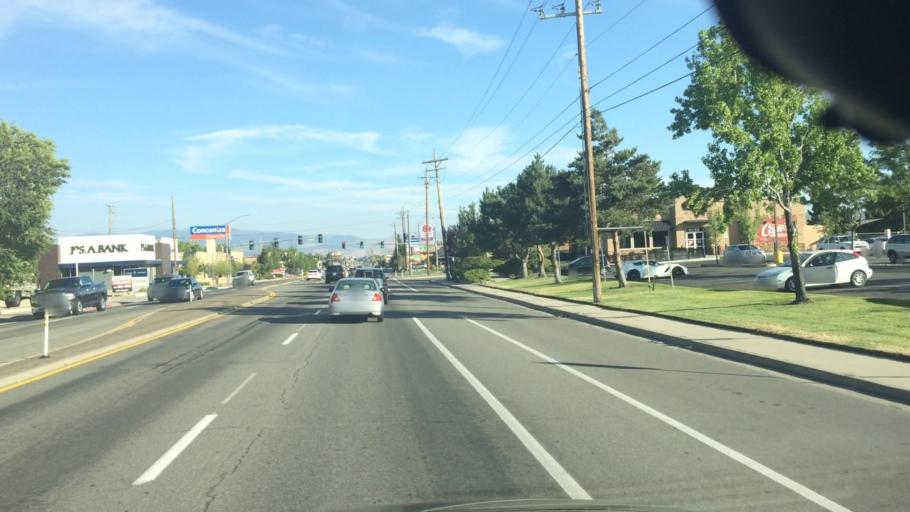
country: US
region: Nevada
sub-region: Washoe County
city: Reno
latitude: 39.4692
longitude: -119.7855
